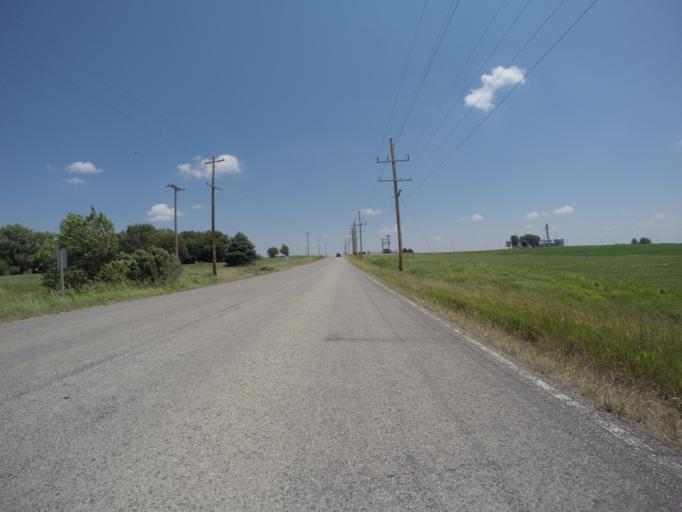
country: US
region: Kansas
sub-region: Doniphan County
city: Troy
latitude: 39.7690
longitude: -95.1002
